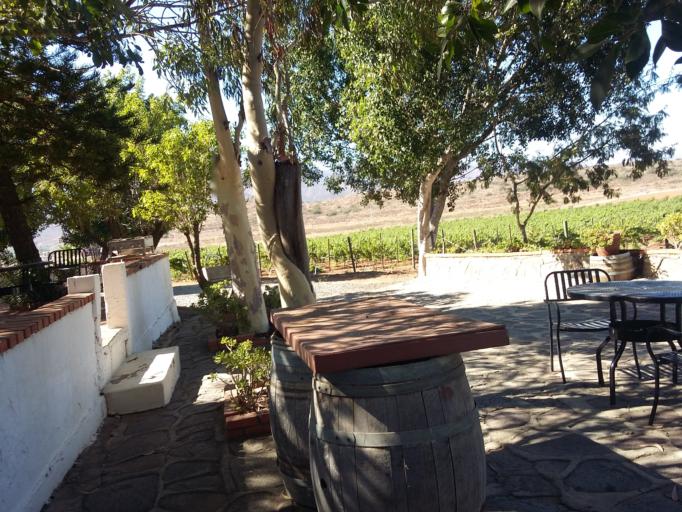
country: MX
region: Baja California
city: El Sauzal
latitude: 32.0018
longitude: -116.6745
